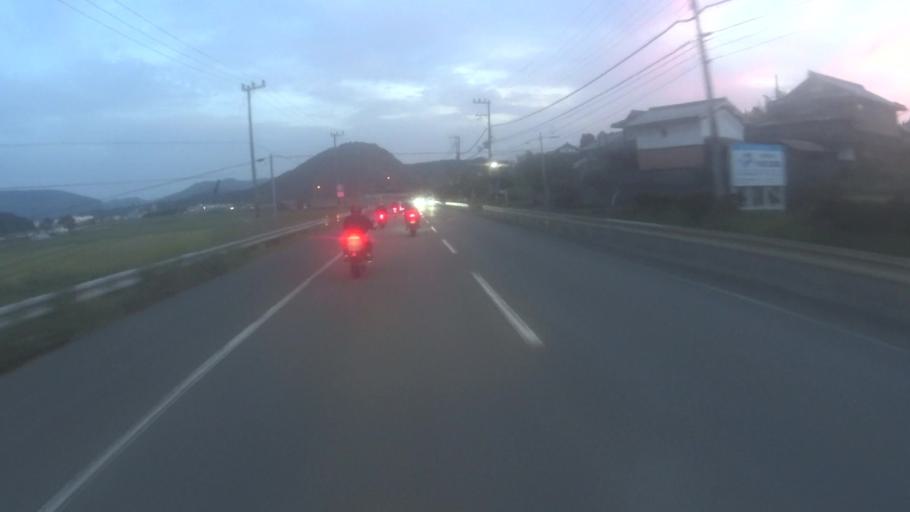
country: JP
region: Kyoto
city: Ayabe
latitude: 35.1900
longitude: 135.4176
